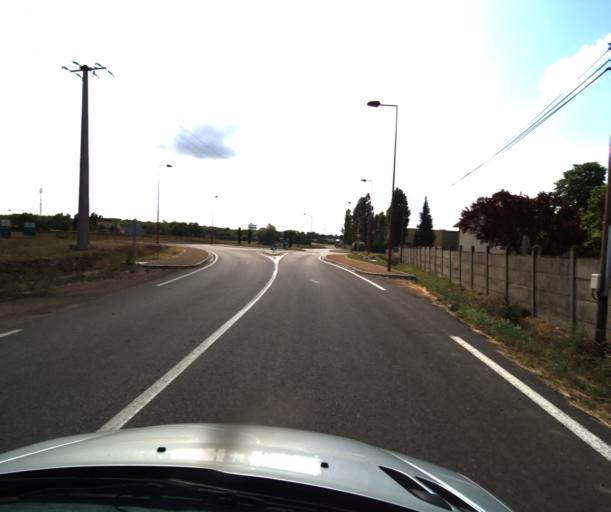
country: FR
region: Midi-Pyrenees
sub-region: Departement du Tarn-et-Garonne
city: Finhan
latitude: 43.9245
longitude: 1.2605
